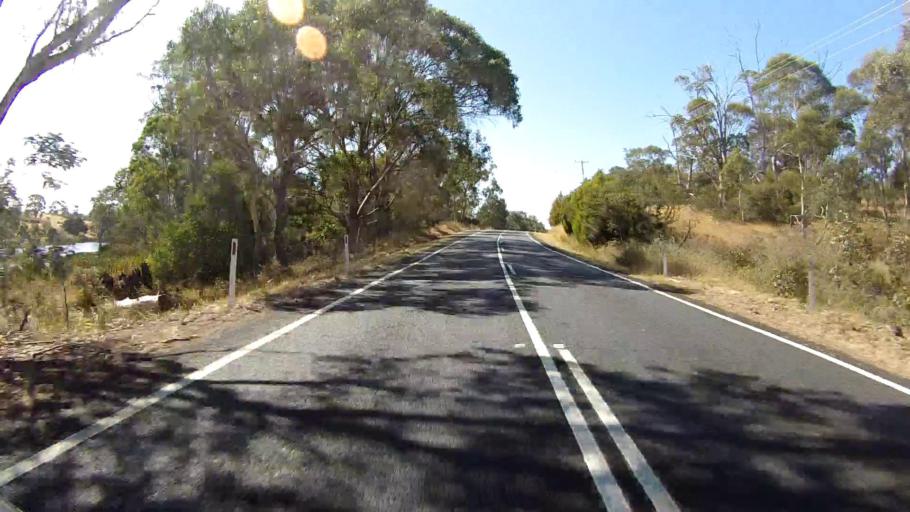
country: AU
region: Tasmania
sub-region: Sorell
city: Sorell
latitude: -42.3895
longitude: 147.9348
